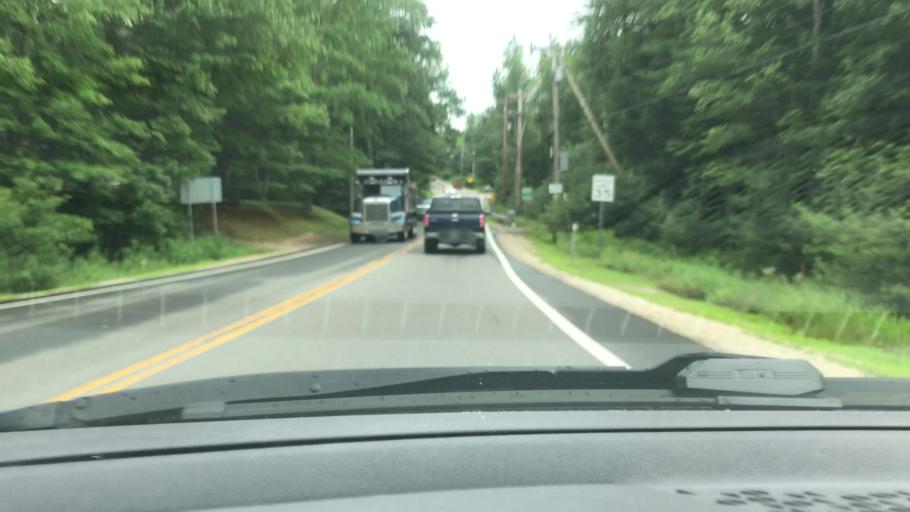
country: US
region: New Hampshire
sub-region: Merrimack County
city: Epsom
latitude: 43.2208
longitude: -71.2916
